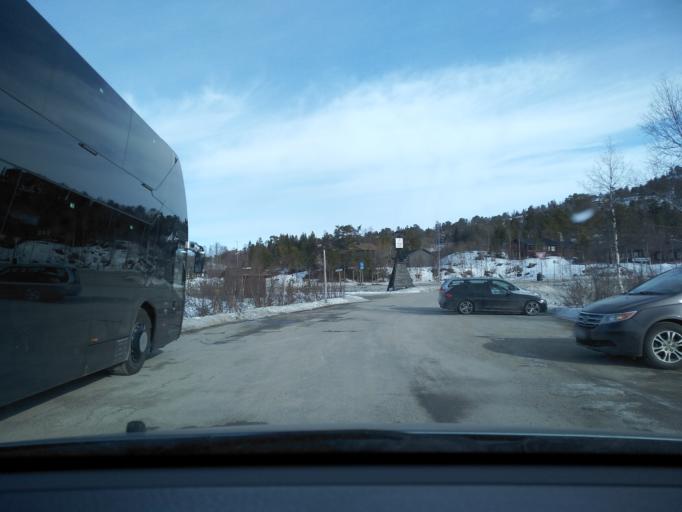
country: NO
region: Aust-Agder
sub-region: Bykle
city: Hovden
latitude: 59.5560
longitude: 7.3597
